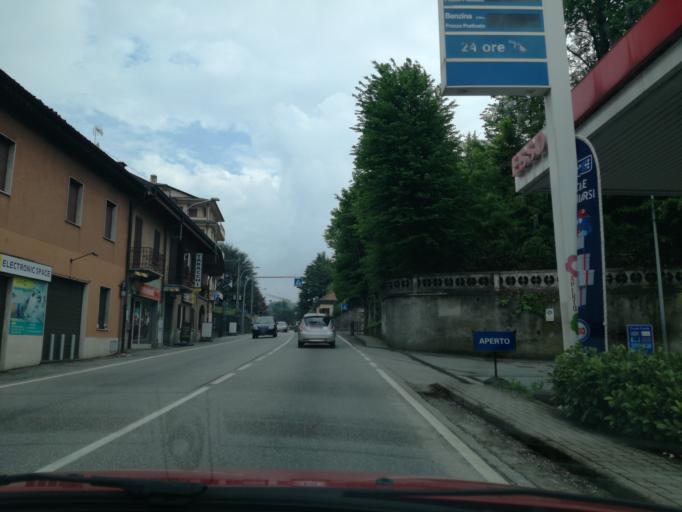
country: IT
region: Lombardy
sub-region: Provincia di Lecco
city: Cernusco Lombardone
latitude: 45.6997
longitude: 9.4082
